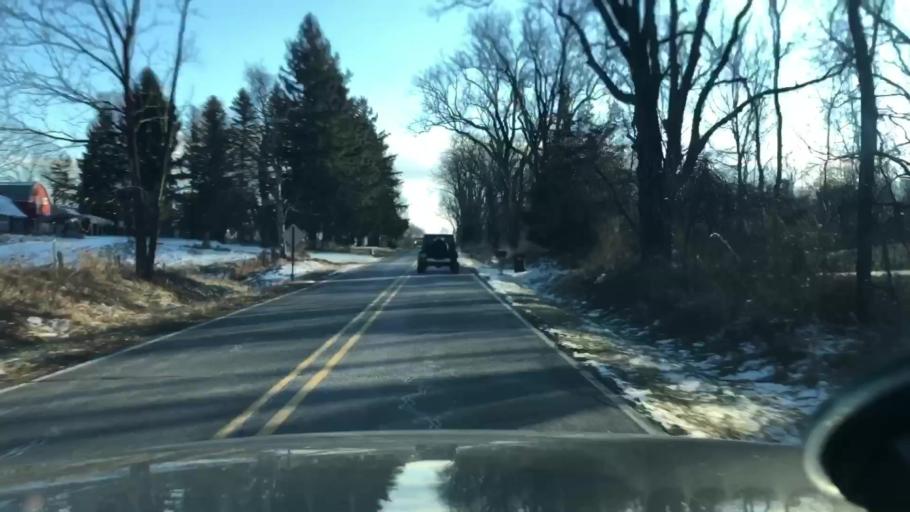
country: US
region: Michigan
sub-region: Jackson County
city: Vandercook Lake
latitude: 42.1225
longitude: -84.4515
